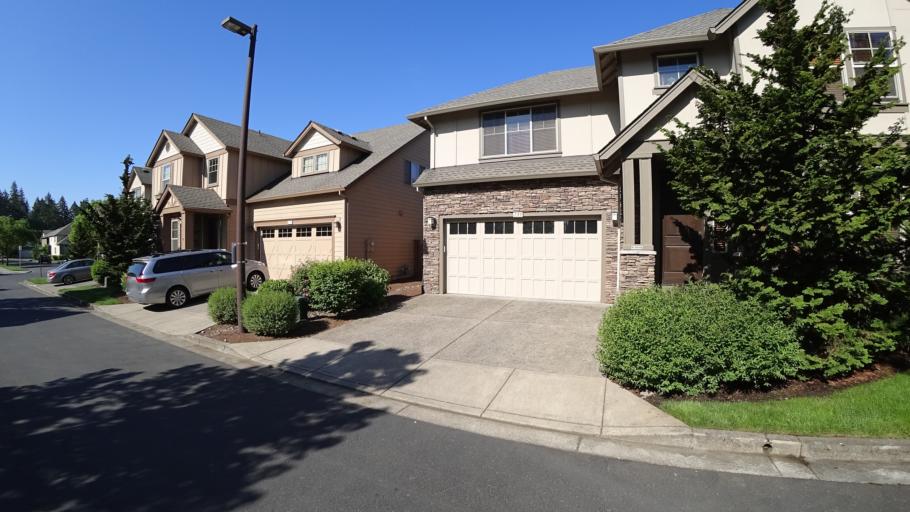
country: US
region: Oregon
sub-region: Washington County
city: Rockcreek
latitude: 45.5230
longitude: -122.9172
